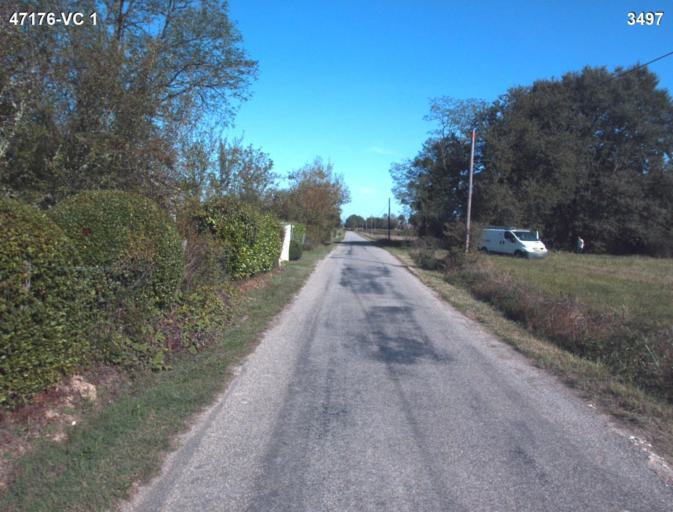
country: FR
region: Aquitaine
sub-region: Departement du Lot-et-Garonne
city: Vianne
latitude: 44.2208
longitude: 0.3061
